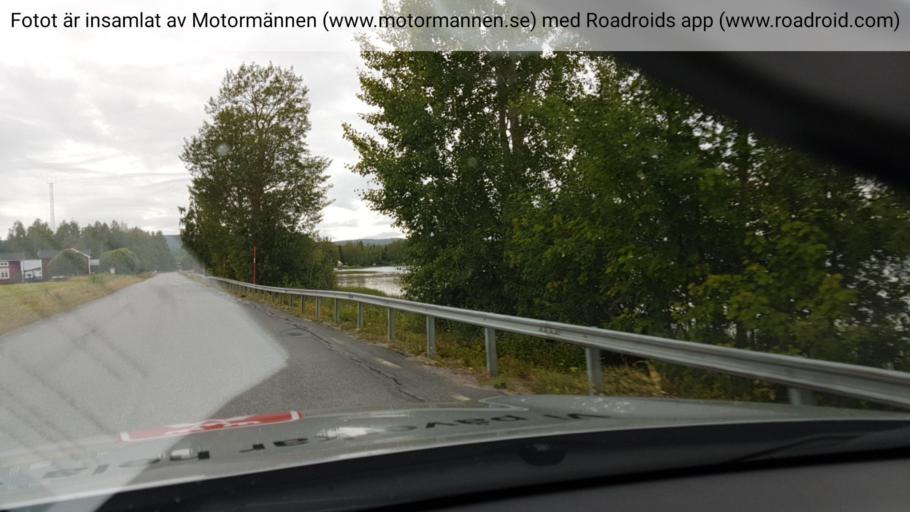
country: SE
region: Norrbotten
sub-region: Bodens Kommun
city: Boden
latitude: 65.8255
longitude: 21.5457
